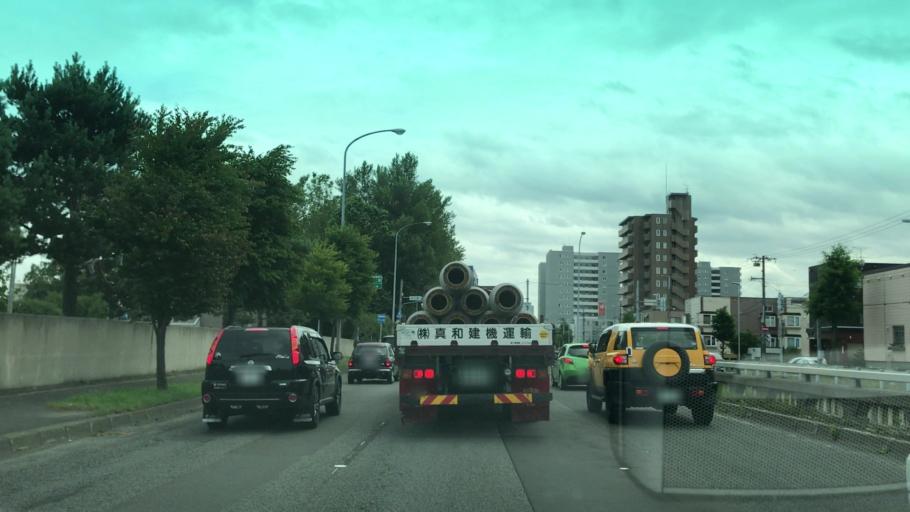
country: JP
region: Hokkaido
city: Sapporo
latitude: 43.0961
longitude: 141.3465
